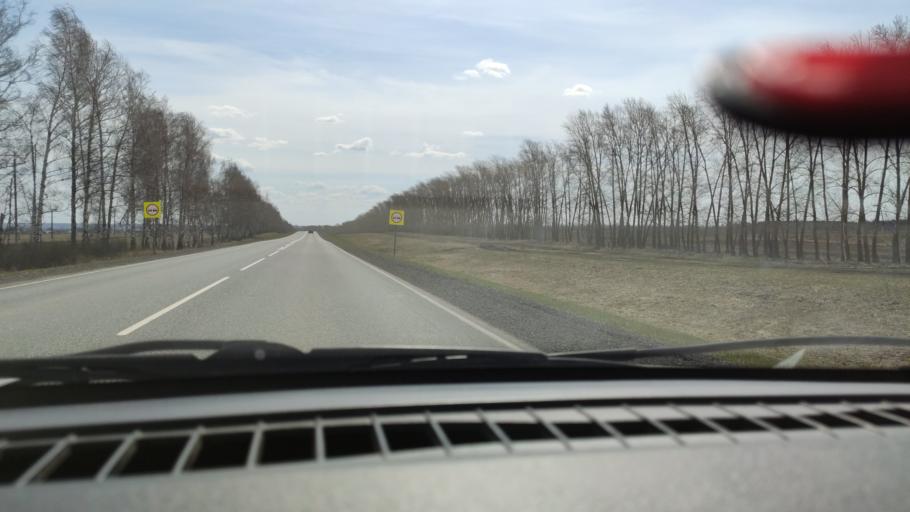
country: RU
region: Bashkortostan
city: Kushnarenkovo
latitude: 55.2127
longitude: 55.0990
